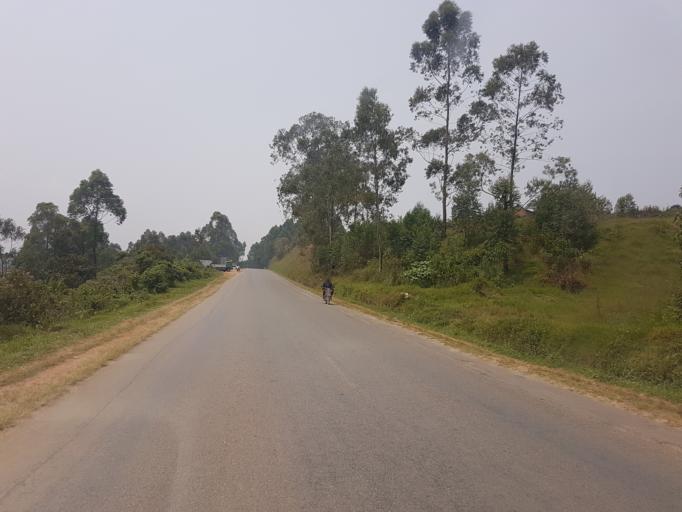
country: UG
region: Western Region
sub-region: Bushenyi District
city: Bushenyi
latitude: -0.5409
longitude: 30.1530
